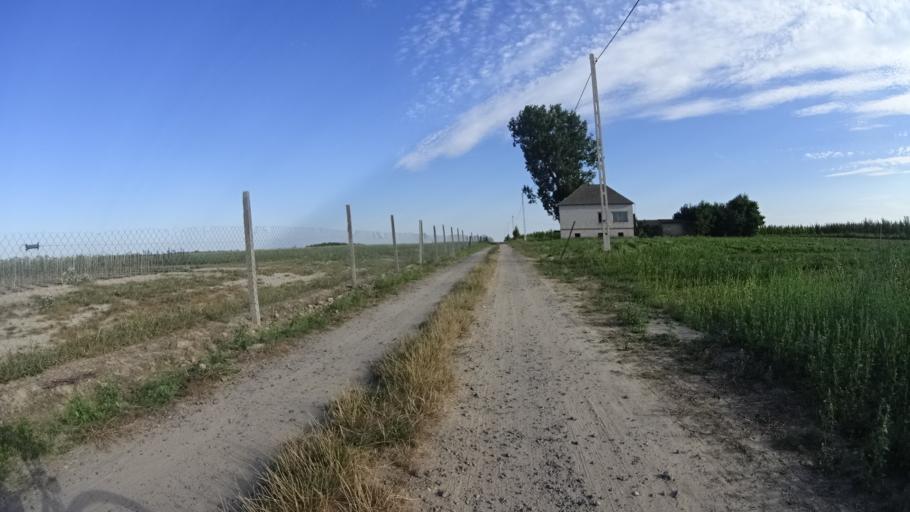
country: PL
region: Masovian Voivodeship
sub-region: Powiat bialobrzeski
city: Wysmierzyce
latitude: 51.6799
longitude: 20.8164
